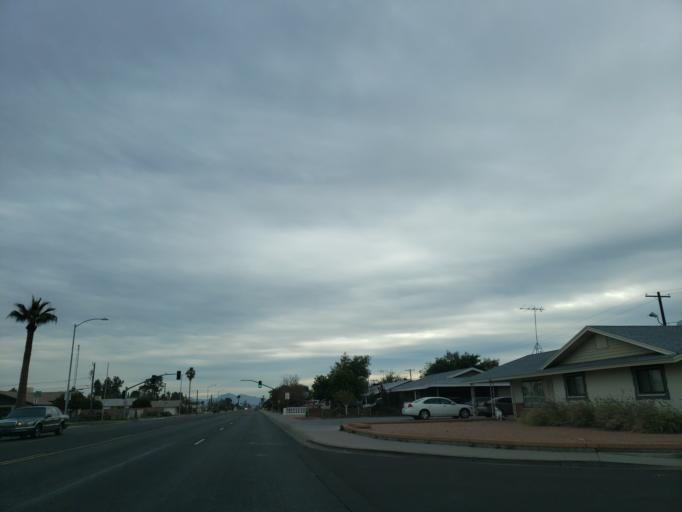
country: US
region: Arizona
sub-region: Maricopa County
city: Youngtown
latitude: 33.6032
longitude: -112.2988
